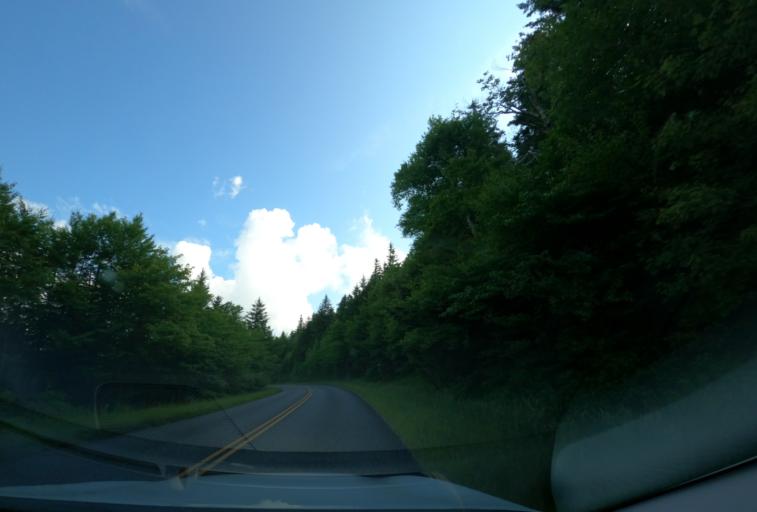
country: US
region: North Carolina
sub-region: Haywood County
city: Hazelwood
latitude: 35.3278
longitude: -82.9649
